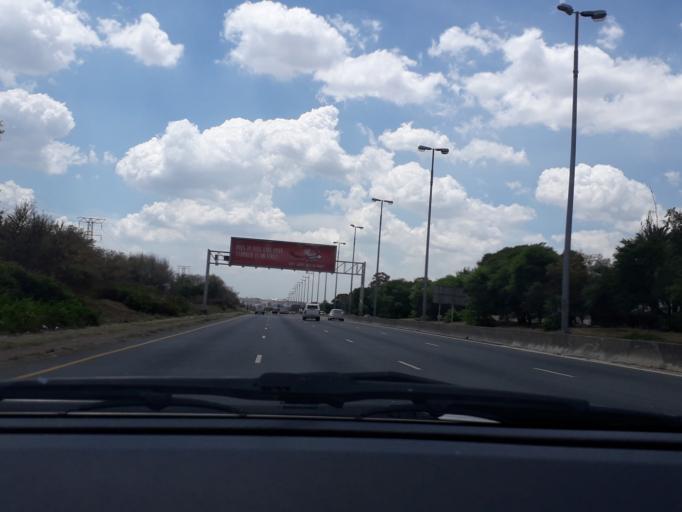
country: ZA
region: Gauteng
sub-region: City of Johannesburg Metropolitan Municipality
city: Johannesburg
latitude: -26.2477
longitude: 28.0018
